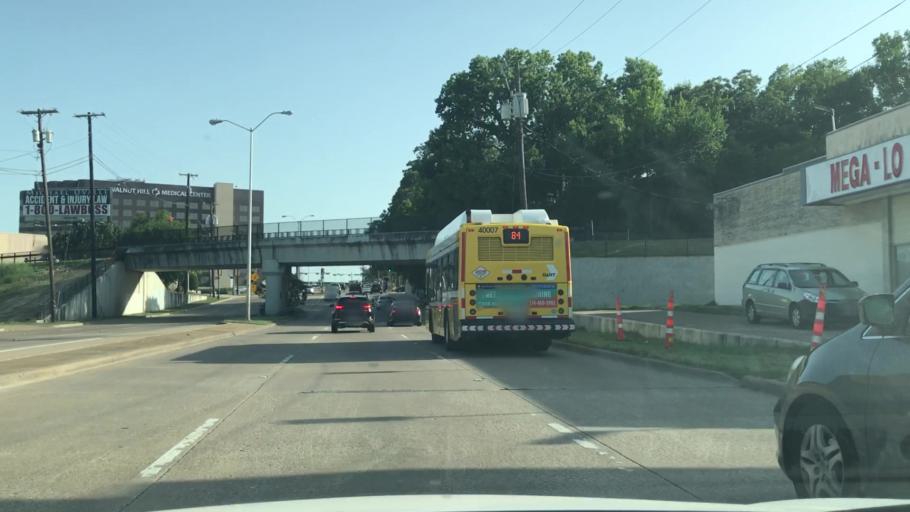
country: US
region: Texas
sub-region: Dallas County
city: University Park
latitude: 32.8869
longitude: -96.7579
